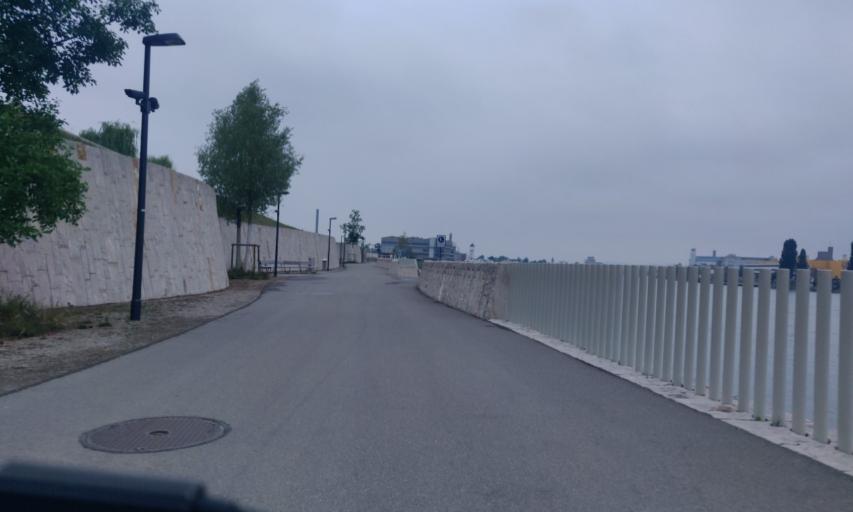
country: CH
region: Basel-City
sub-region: Basel-Stadt
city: Basel
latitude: 47.5746
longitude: 7.5833
